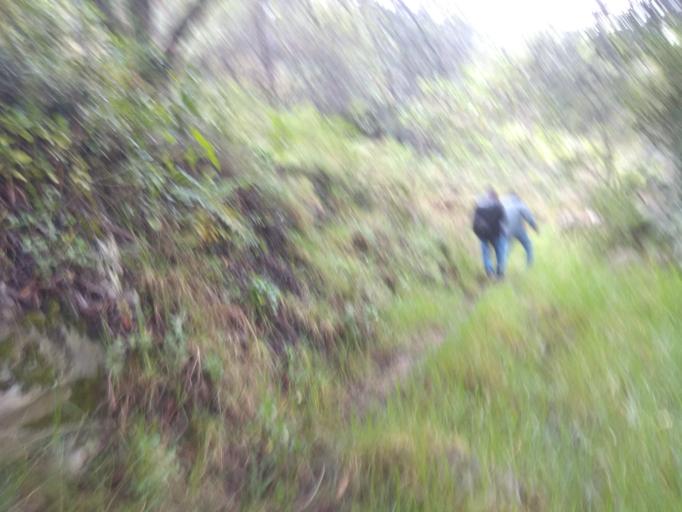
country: CO
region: Boyaca
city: Socha Viejo
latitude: 5.9859
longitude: -72.7024
